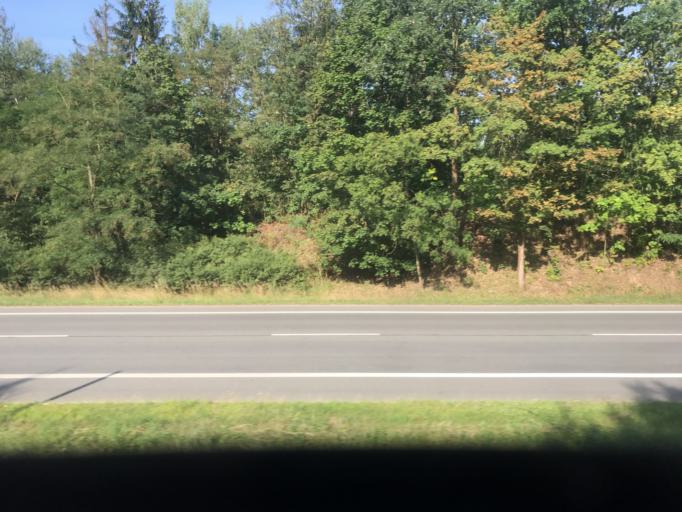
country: CZ
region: Jihocesky
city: Plana nad Luznici
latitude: 49.3425
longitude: 14.7112
